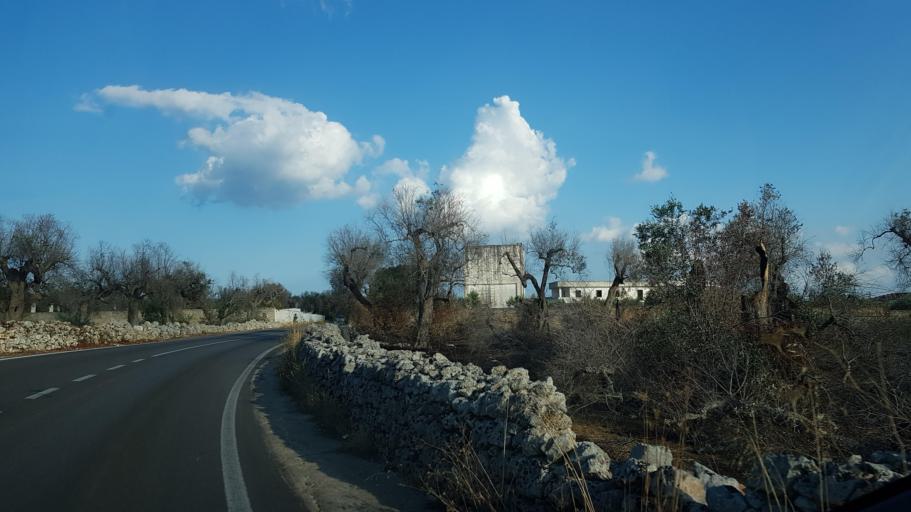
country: IT
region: Apulia
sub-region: Provincia di Lecce
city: Castiglione
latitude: 39.9856
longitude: 18.3612
